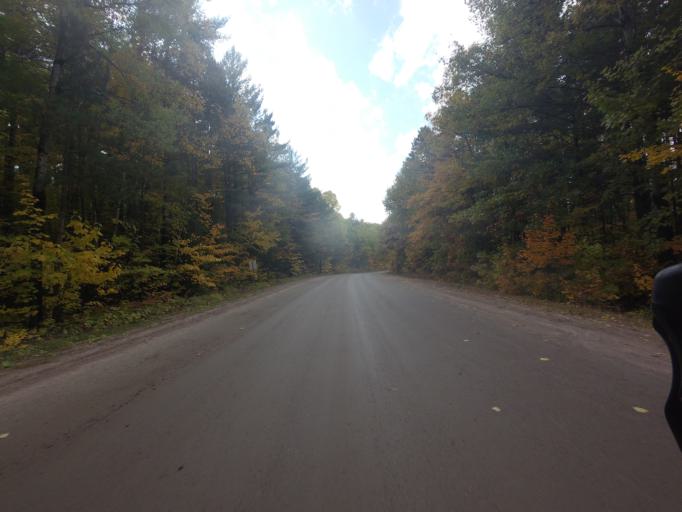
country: CA
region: Ontario
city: Deep River
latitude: 45.8549
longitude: -77.5483
